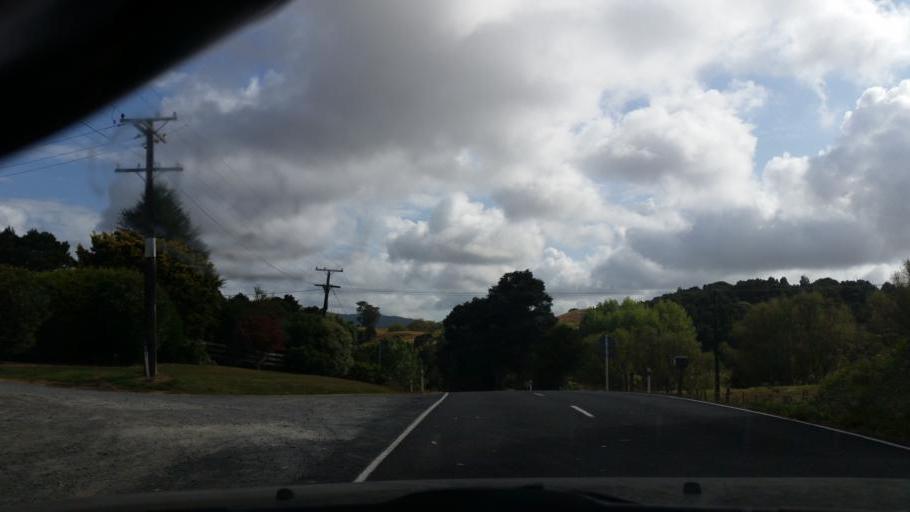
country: NZ
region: Auckland
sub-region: Auckland
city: Wellsford
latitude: -36.1565
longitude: 174.4628
